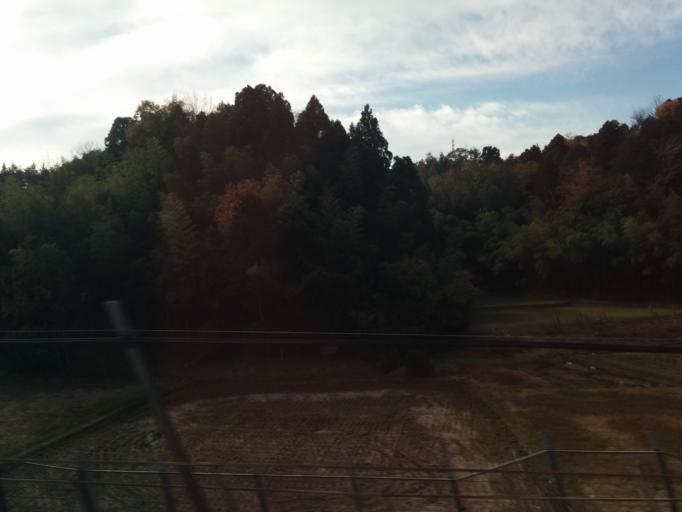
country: JP
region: Shiga Prefecture
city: Hikone
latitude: 35.2672
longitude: 136.2791
